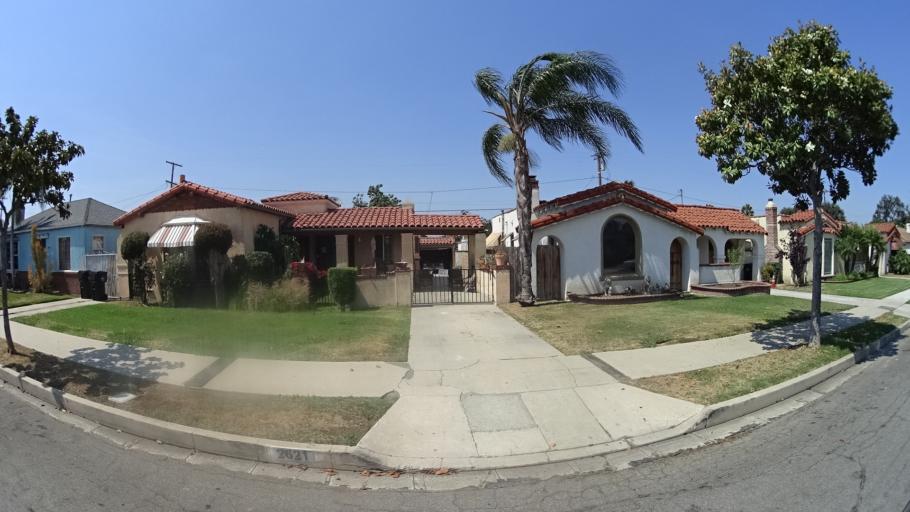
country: US
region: California
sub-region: Los Angeles County
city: Inglewood
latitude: 33.9650
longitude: -118.3230
